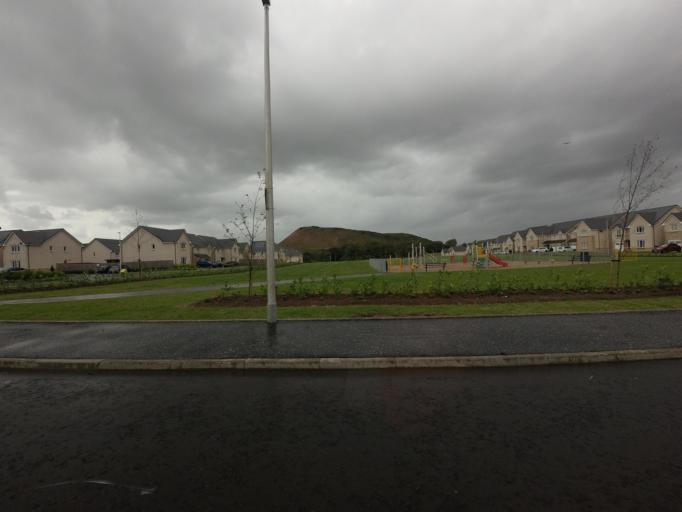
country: GB
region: Scotland
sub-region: West Lothian
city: West Calder
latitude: 55.8562
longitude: -3.5741
